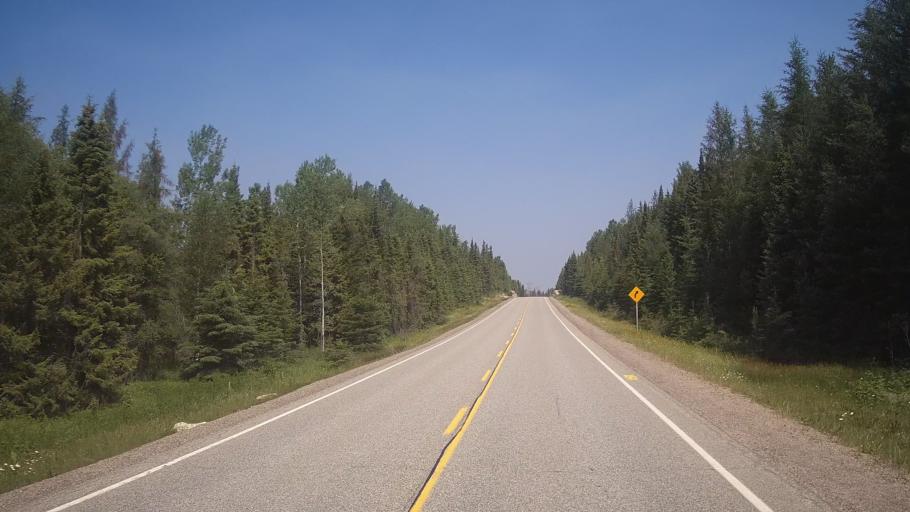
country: CA
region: Ontario
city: Timmins
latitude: 48.0415
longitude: -81.5834
